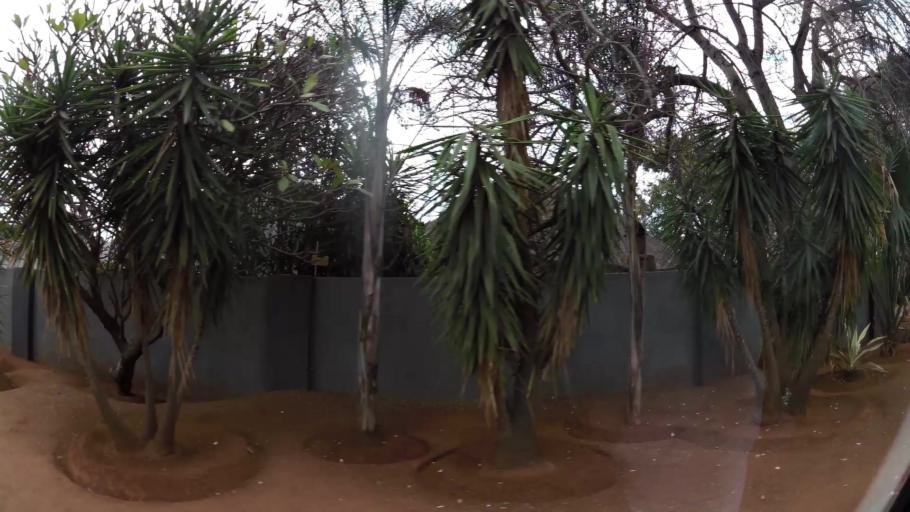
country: ZA
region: Limpopo
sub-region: Waterberg District Municipality
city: Modimolle
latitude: -24.5231
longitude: 28.7072
